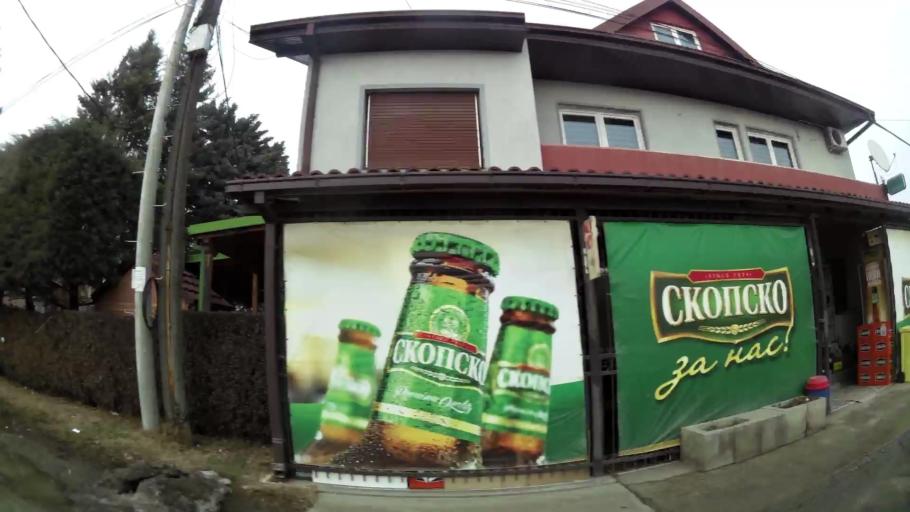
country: MK
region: Ilinden
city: Ilinden
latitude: 41.9971
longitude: 21.5768
